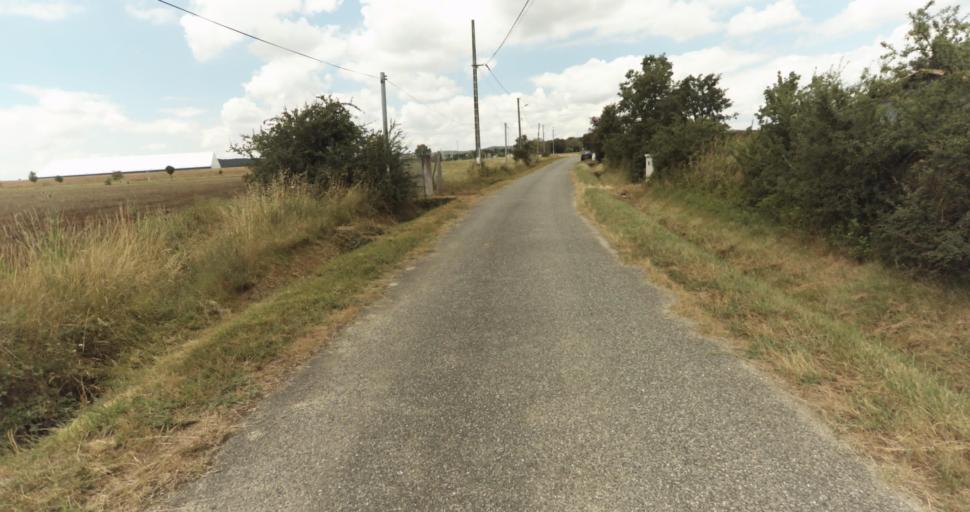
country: FR
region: Midi-Pyrenees
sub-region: Departement de la Haute-Garonne
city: Fontenilles
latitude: 43.5544
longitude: 1.1815
